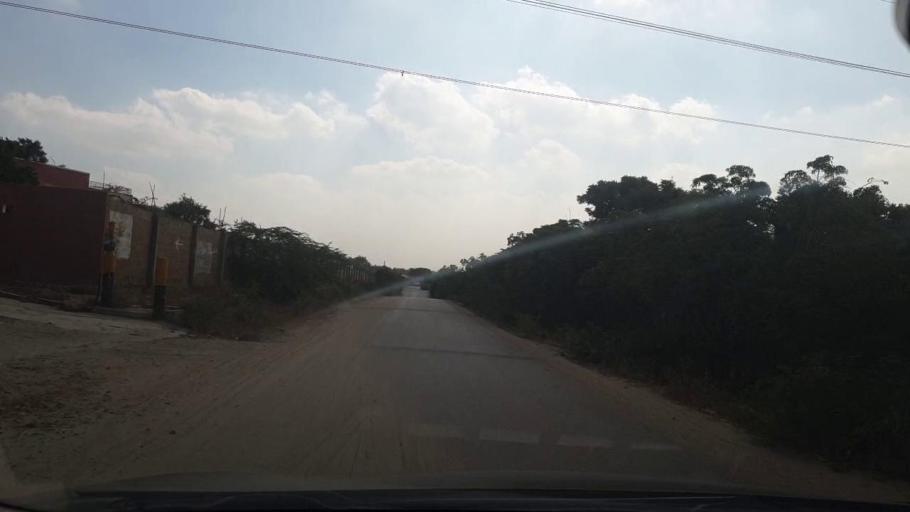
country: PK
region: Sindh
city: Malir Cantonment
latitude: 25.0098
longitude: 67.3550
